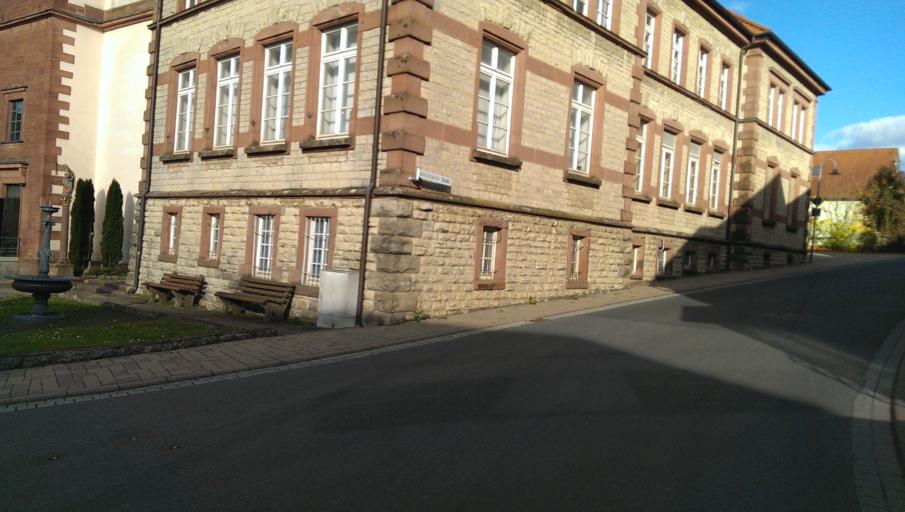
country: DE
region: Baden-Wuerttemberg
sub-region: Karlsruhe Region
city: Rosenberg
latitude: 49.5188
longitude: 9.4439
